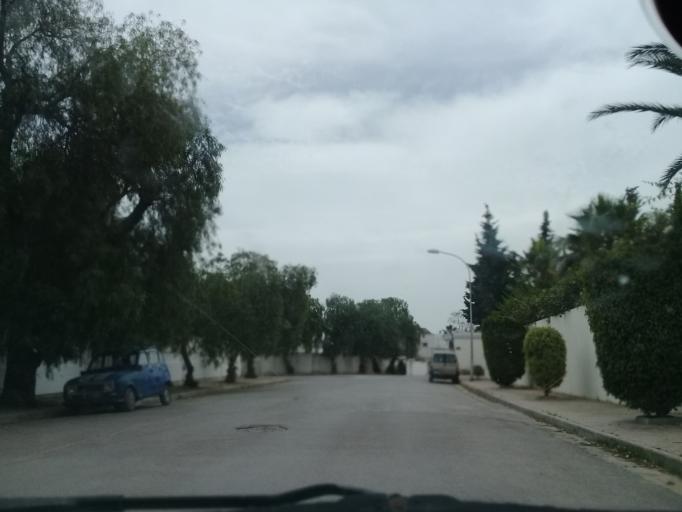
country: TN
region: Tunis
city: Tunis
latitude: 36.8411
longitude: 10.1643
